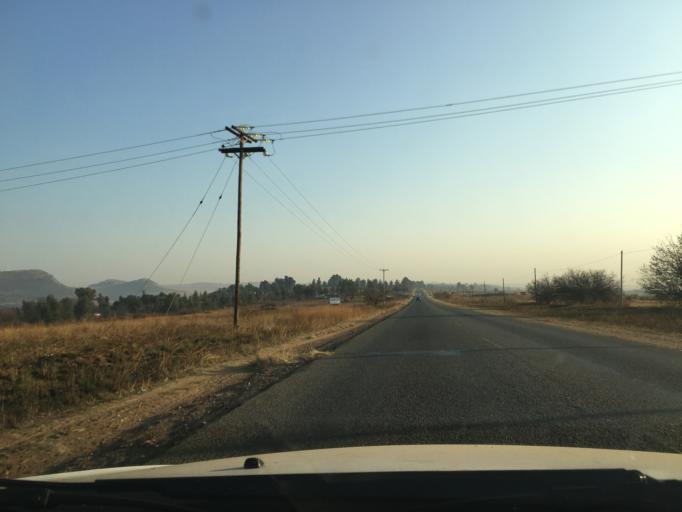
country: ZA
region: Gauteng
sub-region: West Rand District Municipality
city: Muldersdriseloop
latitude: -26.0080
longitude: 27.8584
